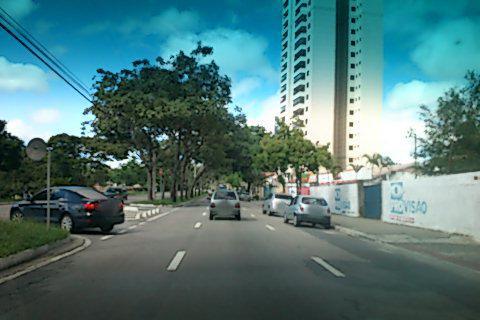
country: BR
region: Sao Paulo
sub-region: Sao Jose Dos Campos
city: Sao Jose dos Campos
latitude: -23.2395
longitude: -45.8815
